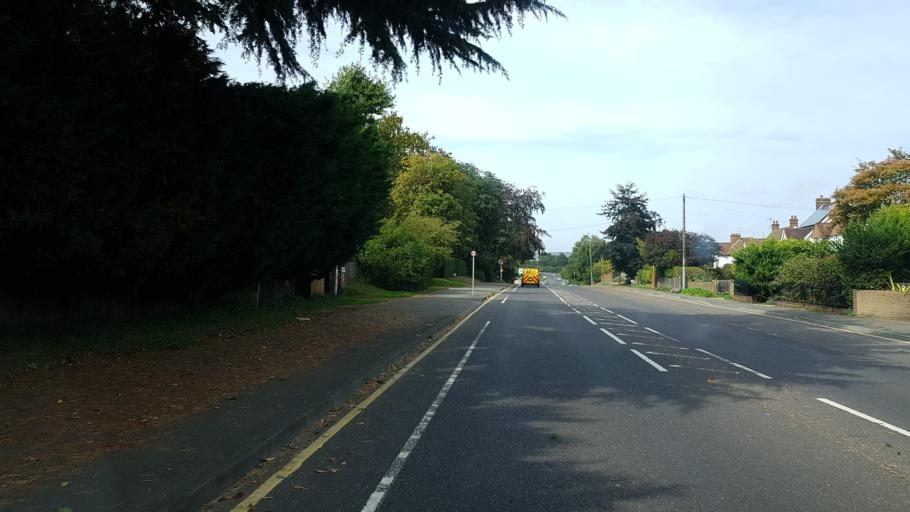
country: GB
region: England
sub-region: Kent
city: West Malling
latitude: 51.2990
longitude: 0.4096
